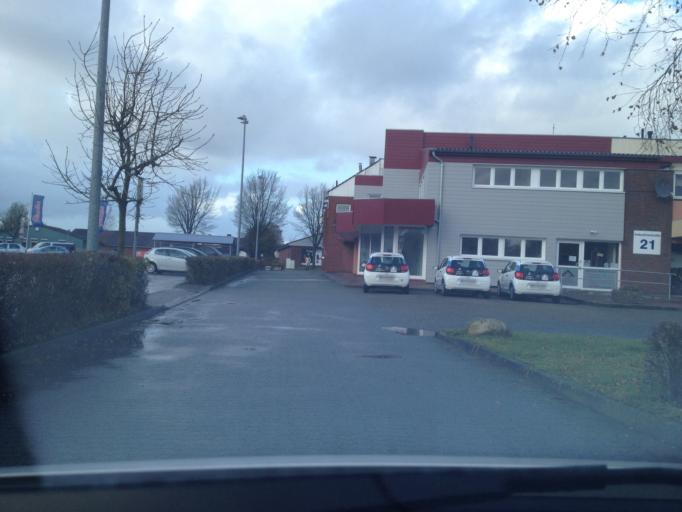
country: DE
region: Schleswig-Holstein
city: Leck
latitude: 54.7770
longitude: 8.9820
